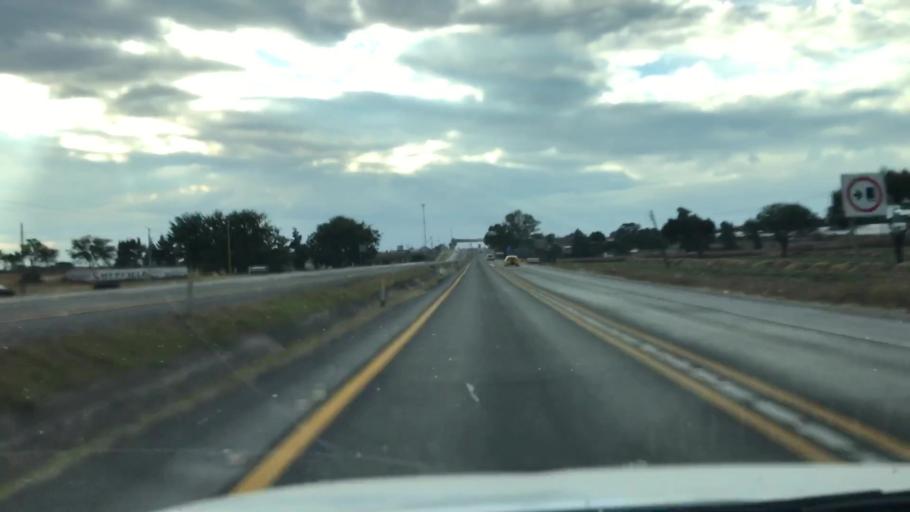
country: MX
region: Guanajuato
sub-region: Penjamo
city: Mezquite de Luna
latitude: 20.3803
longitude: -101.8277
